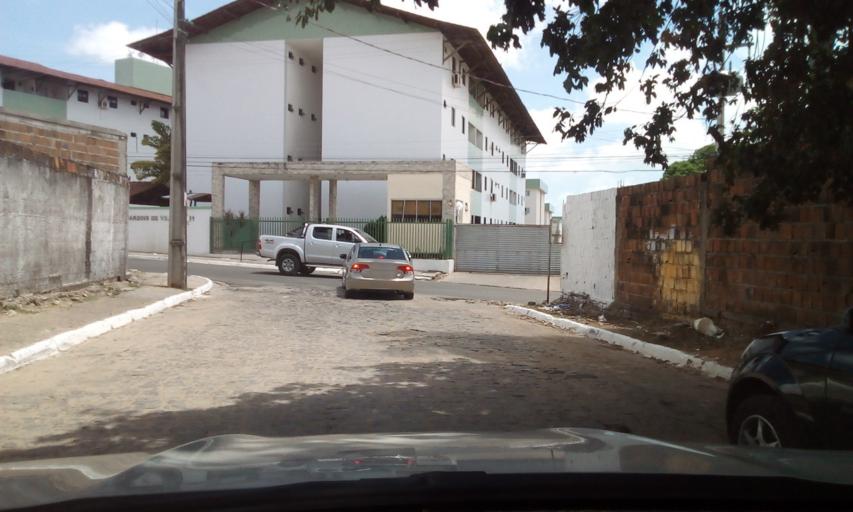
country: BR
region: Paraiba
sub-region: Joao Pessoa
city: Joao Pessoa
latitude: -7.1872
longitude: -34.8701
